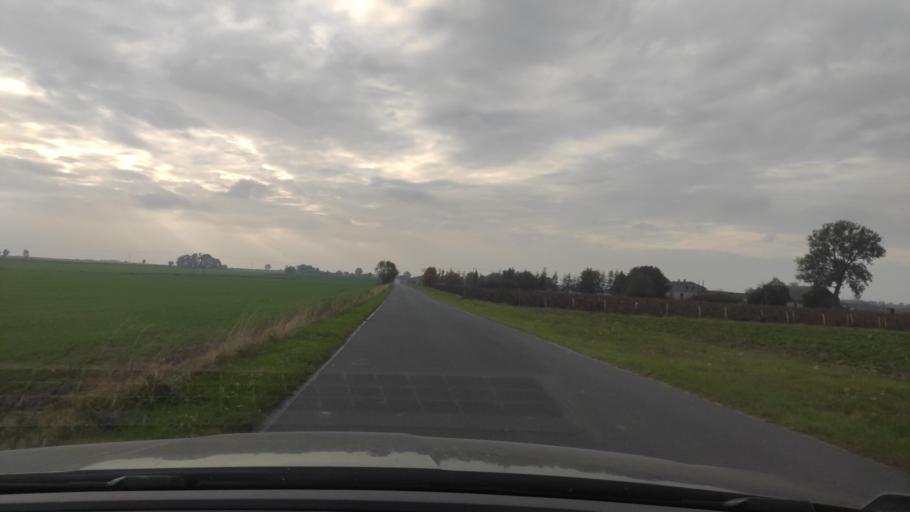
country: PL
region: Greater Poland Voivodeship
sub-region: Powiat poznanski
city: Kostrzyn
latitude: 52.4439
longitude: 17.1962
